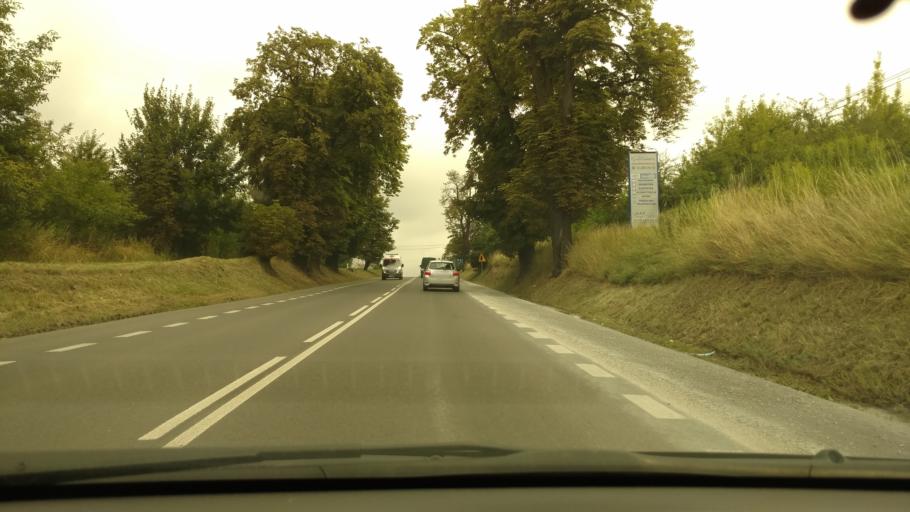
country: PL
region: Lesser Poland Voivodeship
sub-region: Powiat krakowski
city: Zielonki
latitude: 50.1076
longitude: 19.9653
